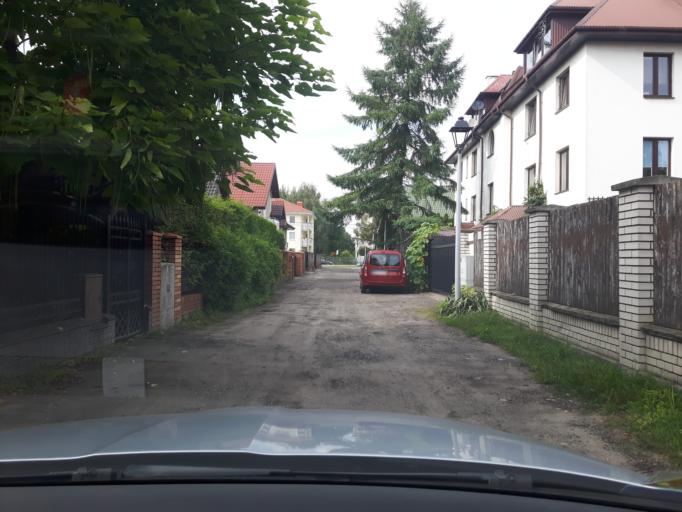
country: PL
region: Masovian Voivodeship
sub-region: Powiat wolominski
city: Zabki
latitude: 52.2783
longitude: 21.1239
